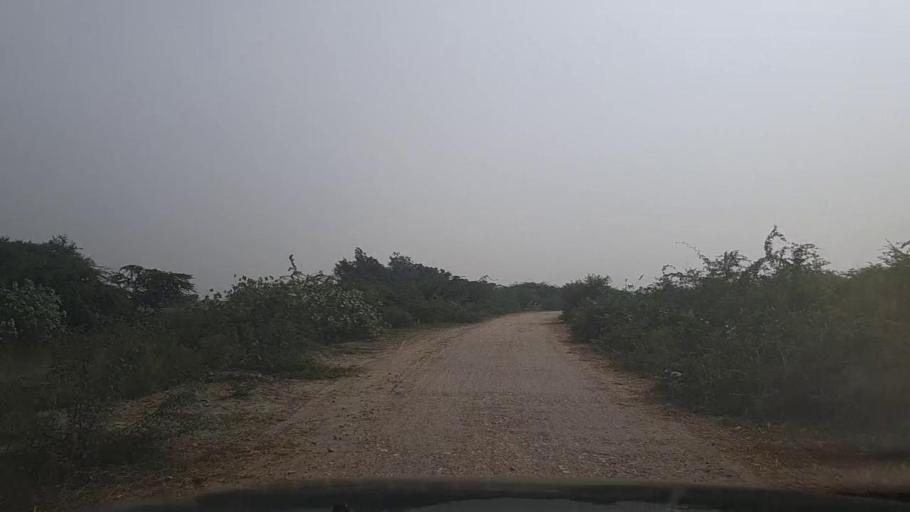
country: PK
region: Sindh
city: Mirpur Sakro
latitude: 24.4841
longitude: 67.6440
